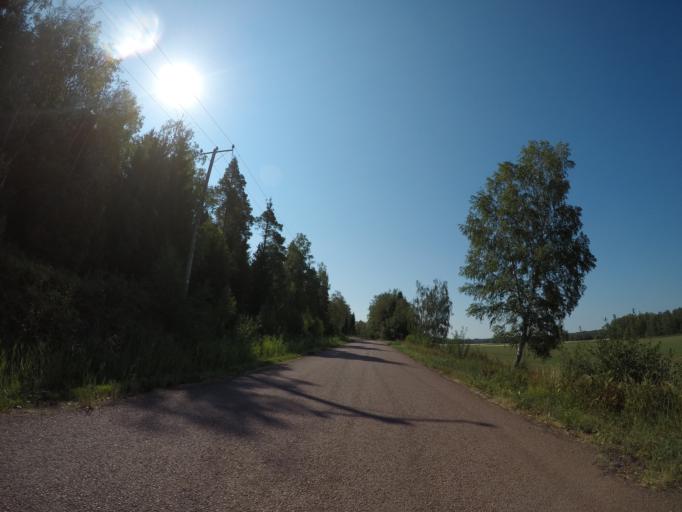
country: AX
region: Alands landsbygd
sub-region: Saltvik
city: Saltvik
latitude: 60.2252
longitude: 20.0104
